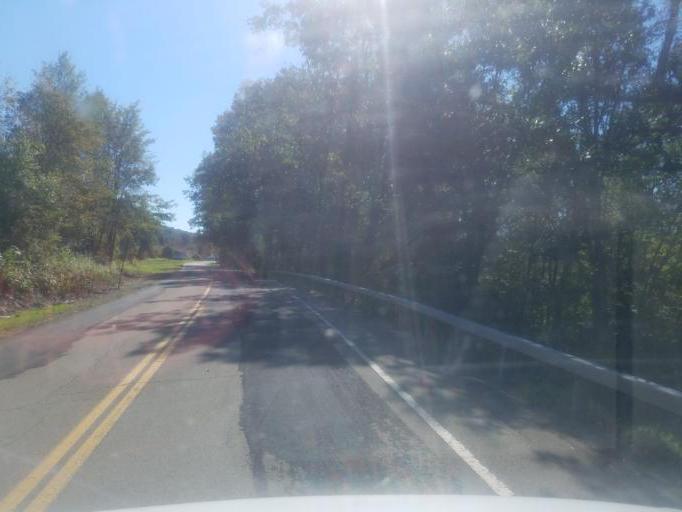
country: US
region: New York
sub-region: Allegany County
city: Friendship
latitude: 42.3137
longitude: -78.1071
